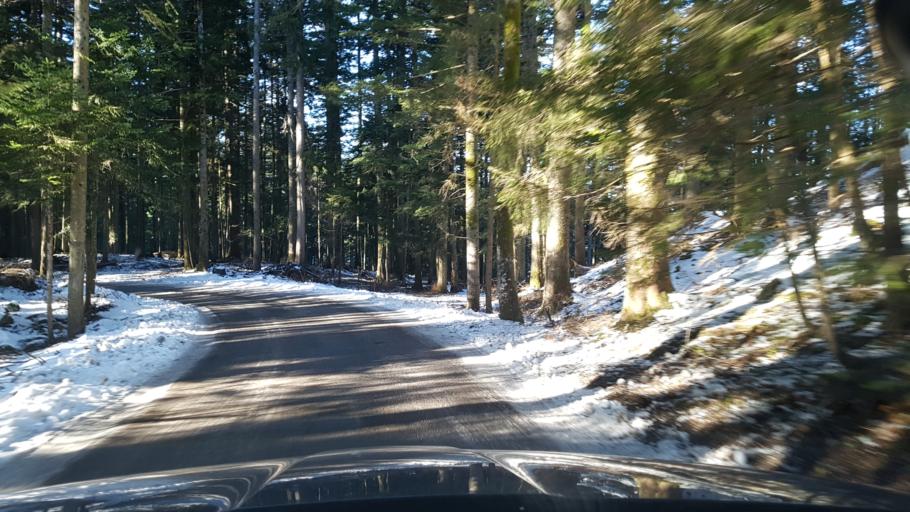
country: AT
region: Salzburg
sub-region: Politischer Bezirk Hallein
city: Scheffau am Tennengebirge
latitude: 47.6345
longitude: 13.2224
